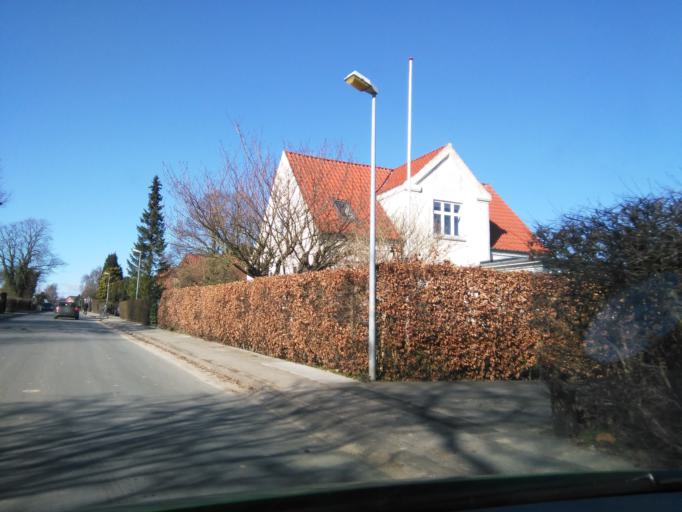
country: DK
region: Central Jutland
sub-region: Arhus Kommune
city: Arhus
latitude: 56.1889
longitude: 10.2230
